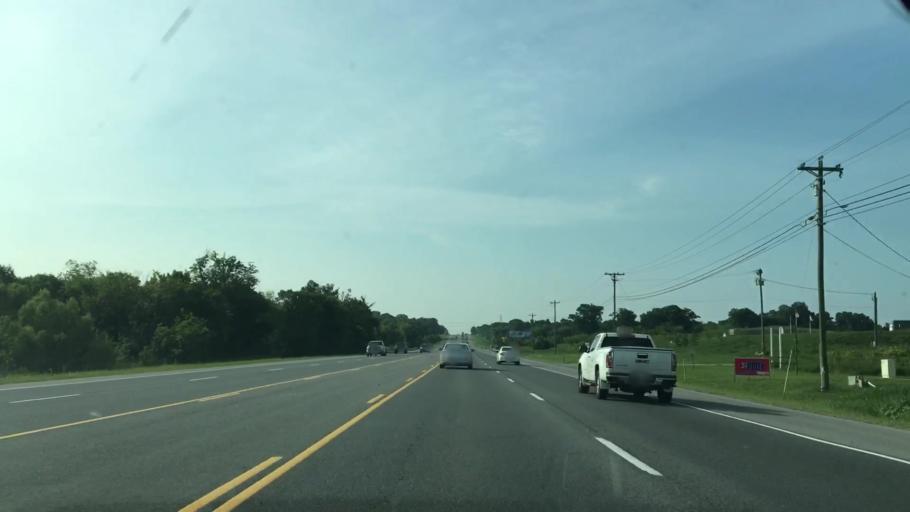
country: US
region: Tennessee
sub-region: Wilson County
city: Mount Juliet
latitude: 36.2222
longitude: -86.4250
